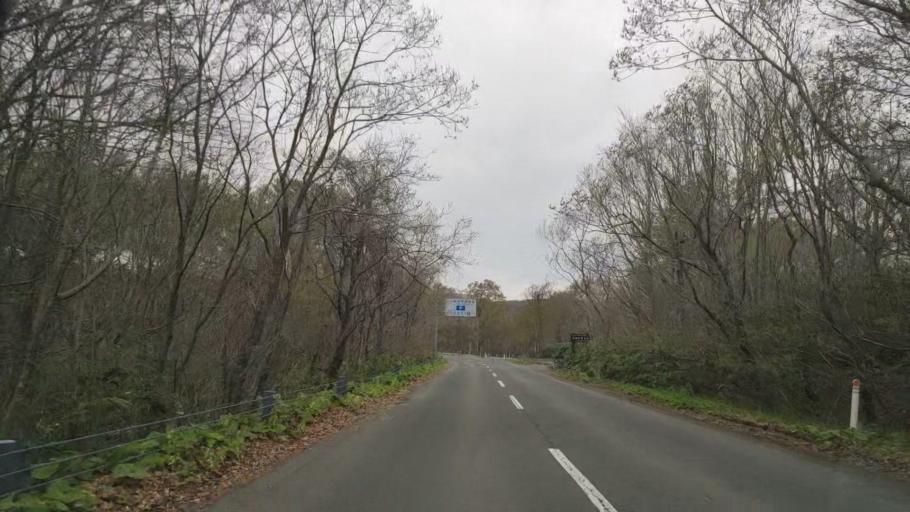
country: JP
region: Akita
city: Hanawa
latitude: 40.4067
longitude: 140.8611
